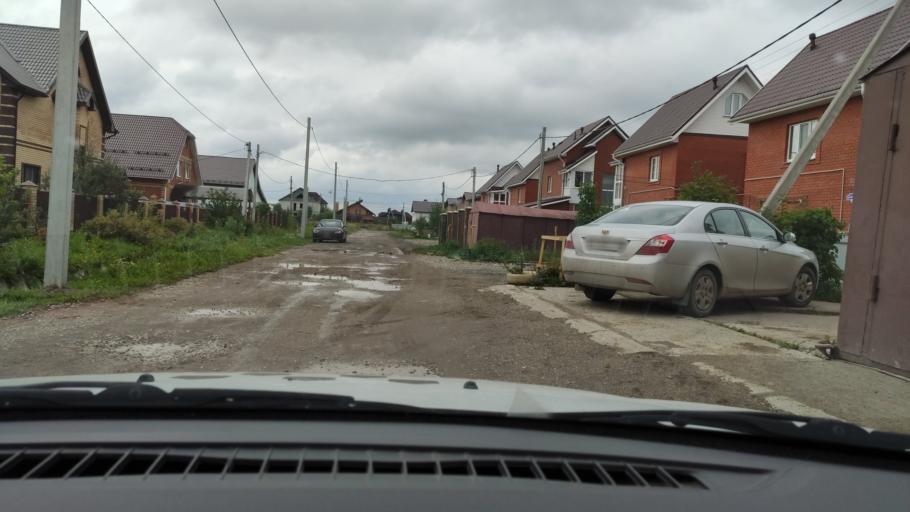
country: RU
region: Perm
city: Perm
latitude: 58.0425
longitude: 56.3788
